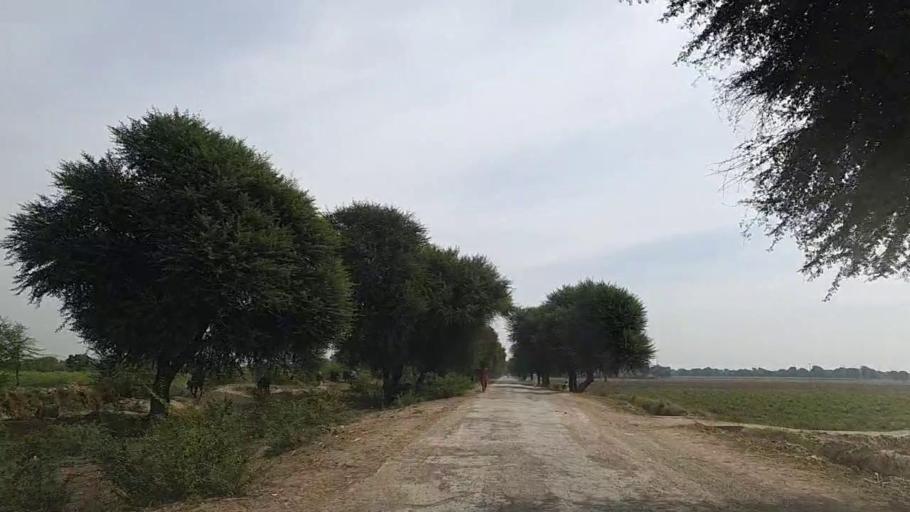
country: PK
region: Sindh
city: Samaro
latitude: 25.2875
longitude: 69.4116
